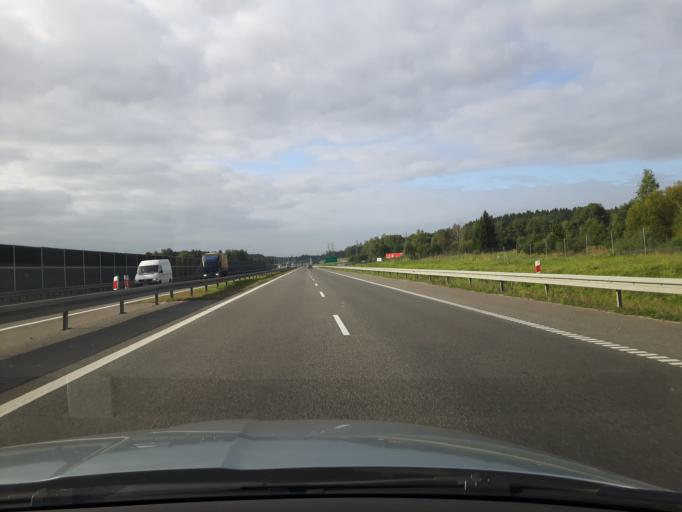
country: PL
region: Swietokrzyskie
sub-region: Powiat skarzyski
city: Suchedniow
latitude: 51.0561
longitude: 20.8269
